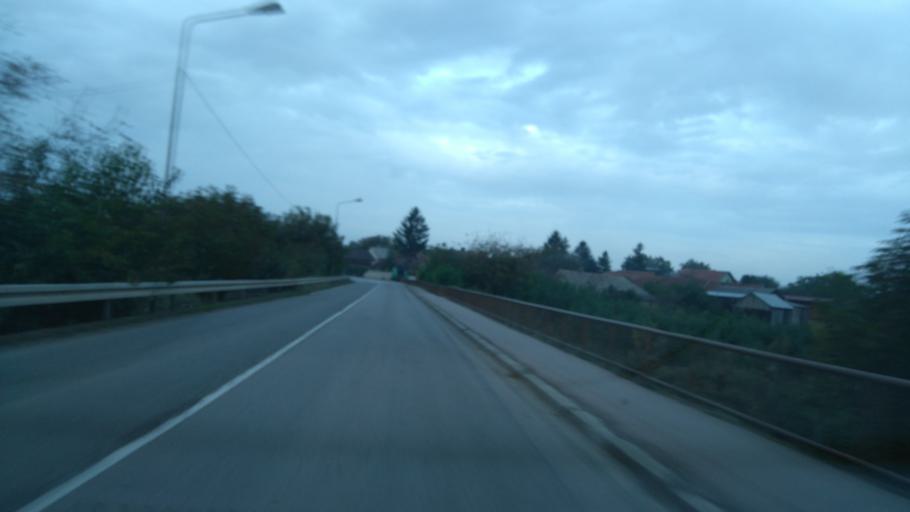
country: RS
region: Autonomna Pokrajina Vojvodina
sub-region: Severnobanatski Okrug
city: Ada
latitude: 45.7883
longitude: 20.1378
